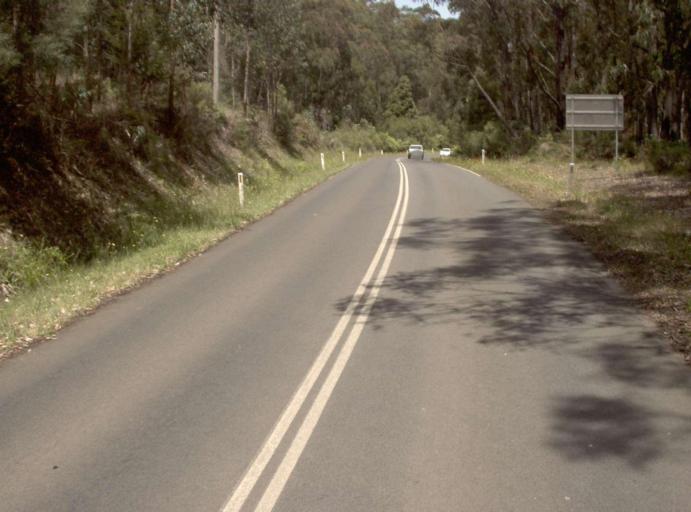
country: AU
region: Victoria
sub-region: Latrobe
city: Moe
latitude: -37.9842
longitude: 146.3686
